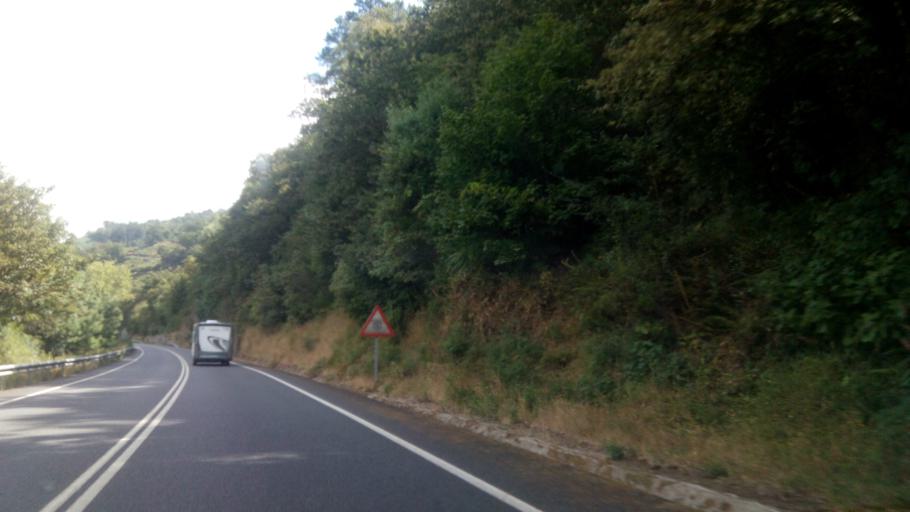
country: ES
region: Galicia
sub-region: Provincia de Ourense
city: Nogueira de Ramuin
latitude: 42.4294
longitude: -7.7559
